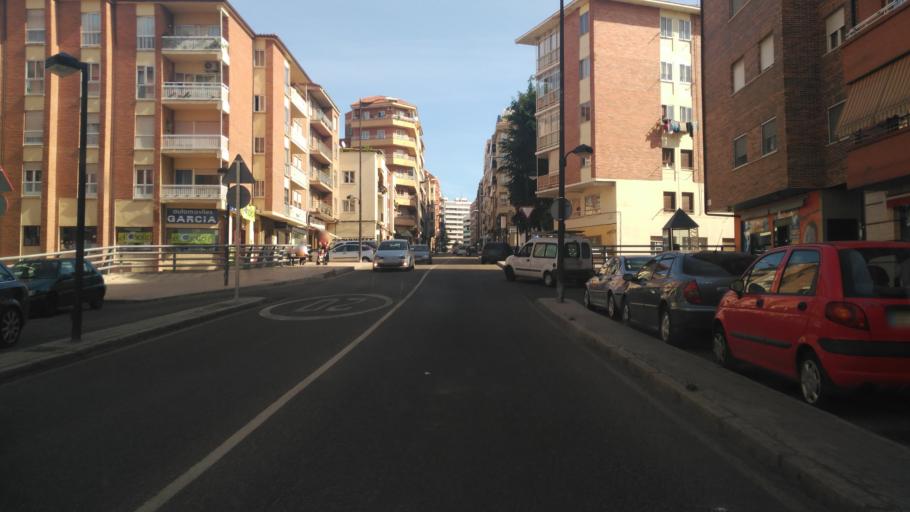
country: ES
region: Castille and Leon
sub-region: Provincia de Zamora
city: Zamora
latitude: 41.5025
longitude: -5.7399
